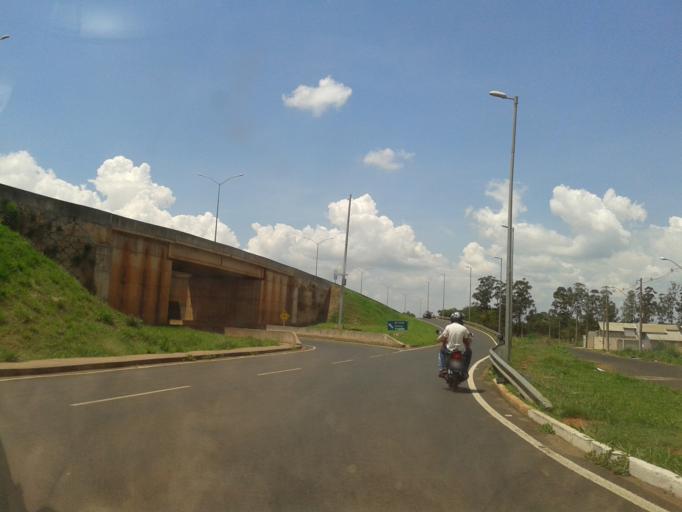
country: BR
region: Minas Gerais
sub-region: Araguari
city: Araguari
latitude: -18.6735
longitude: -48.1784
